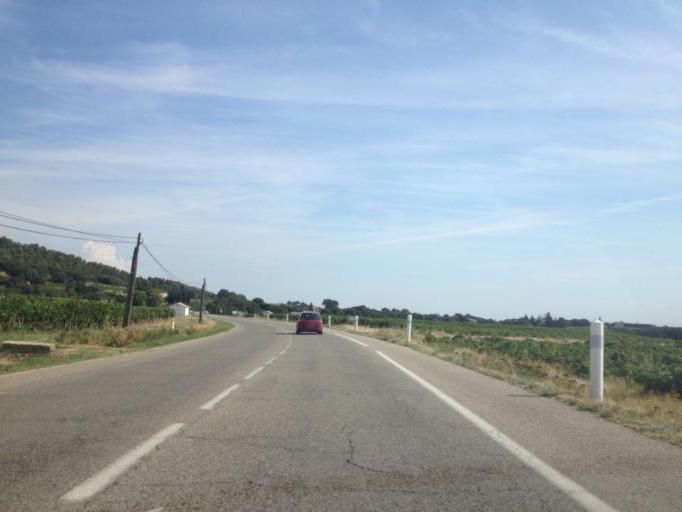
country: FR
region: Provence-Alpes-Cote d'Azur
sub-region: Departement du Vaucluse
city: Vacqueyras
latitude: 44.1536
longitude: 4.9810
